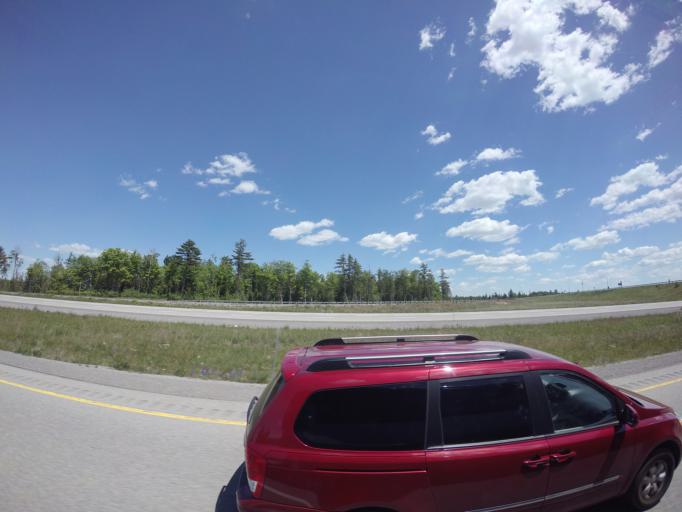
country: CA
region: Ontario
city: Bells Corners
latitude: 45.2507
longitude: -75.9704
